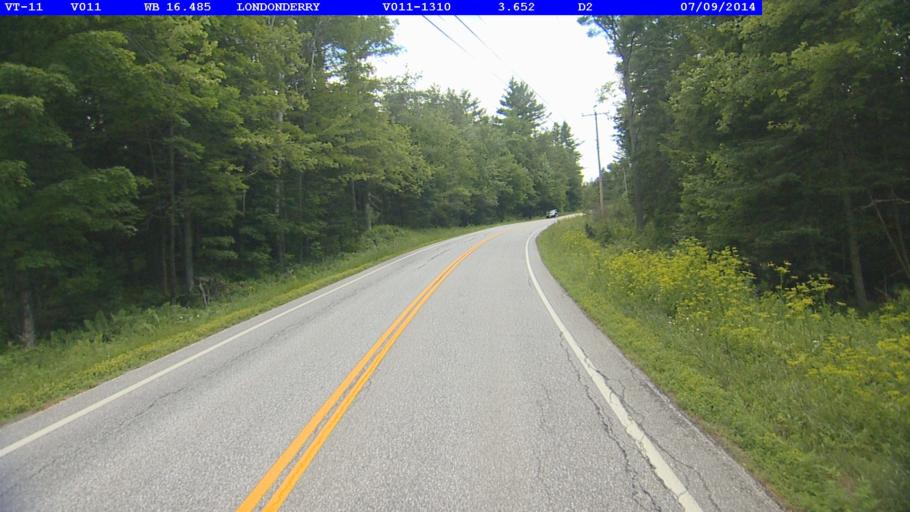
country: US
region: Vermont
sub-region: Windsor County
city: Chester
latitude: 43.2155
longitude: -72.7897
